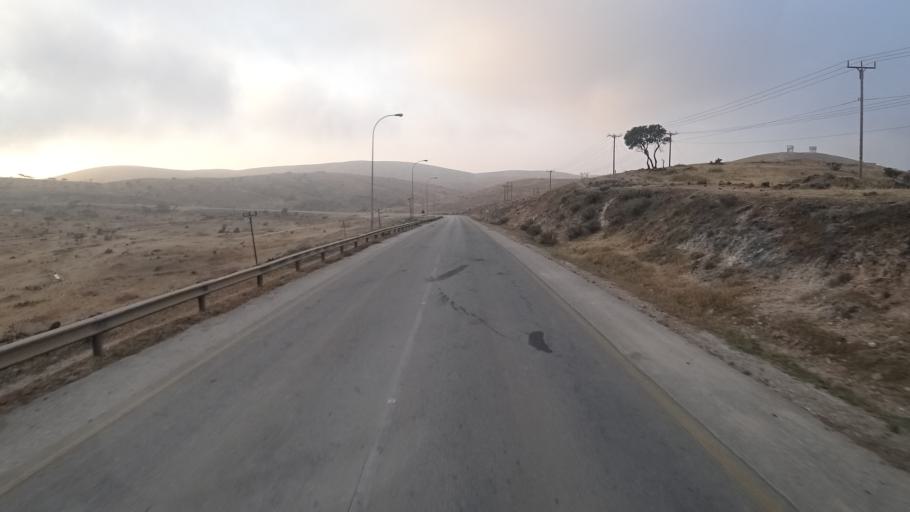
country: OM
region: Zufar
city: Salalah
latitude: 17.1381
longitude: 53.9720
